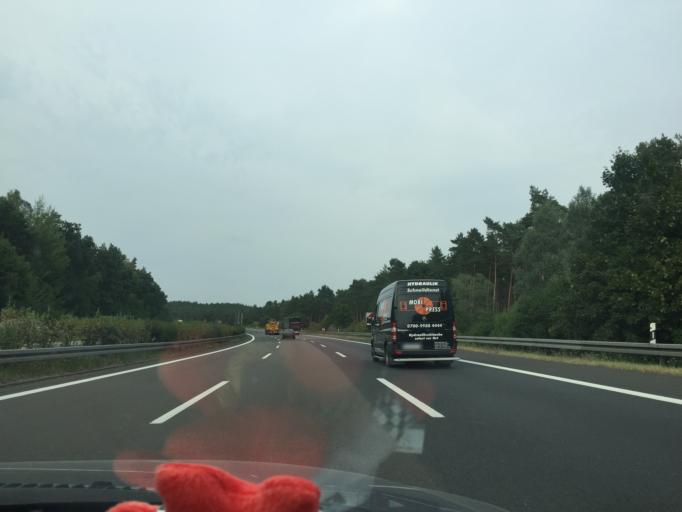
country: DE
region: Brandenburg
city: Grunheide
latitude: 52.4404
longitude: 13.8000
